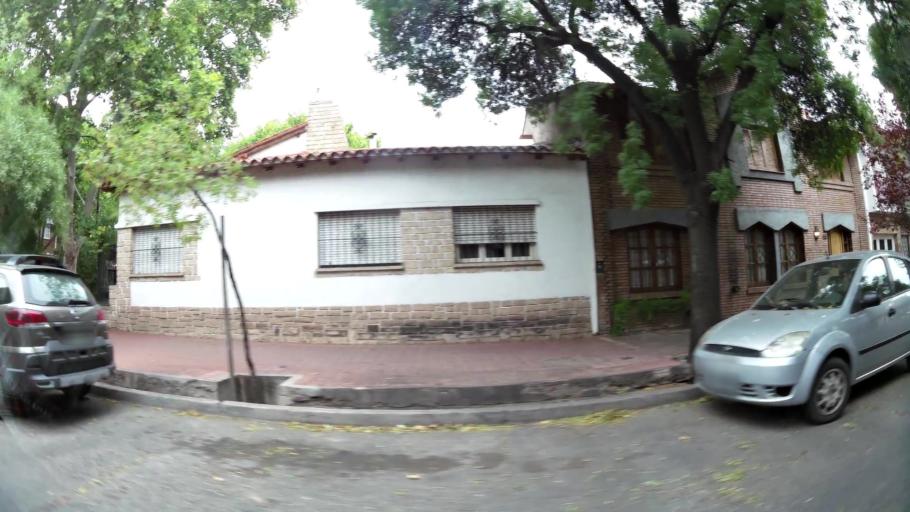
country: AR
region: Mendoza
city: Mendoza
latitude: -32.8864
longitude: -68.8512
